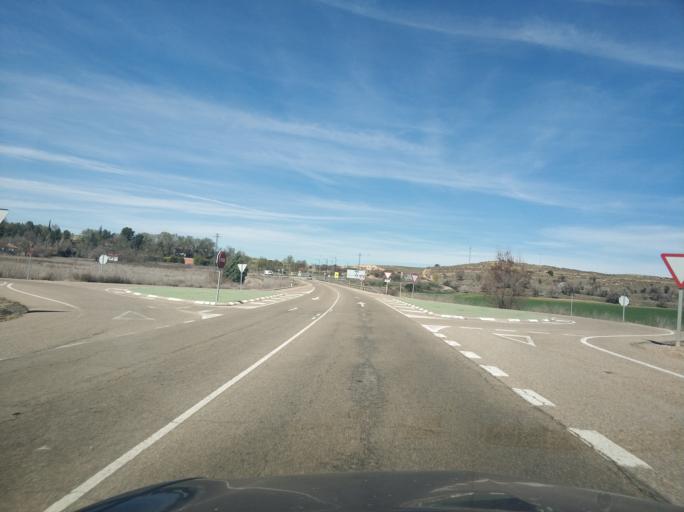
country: ES
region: Castille and Leon
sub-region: Provincia de Valladolid
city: Simancas
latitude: 41.5935
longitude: -4.8184
